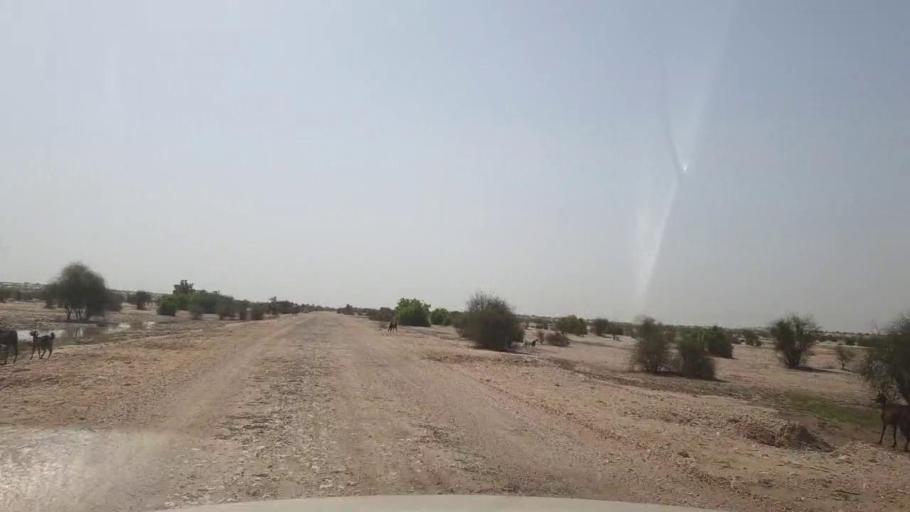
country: PK
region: Sindh
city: Rohri
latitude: 27.4465
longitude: 69.2347
